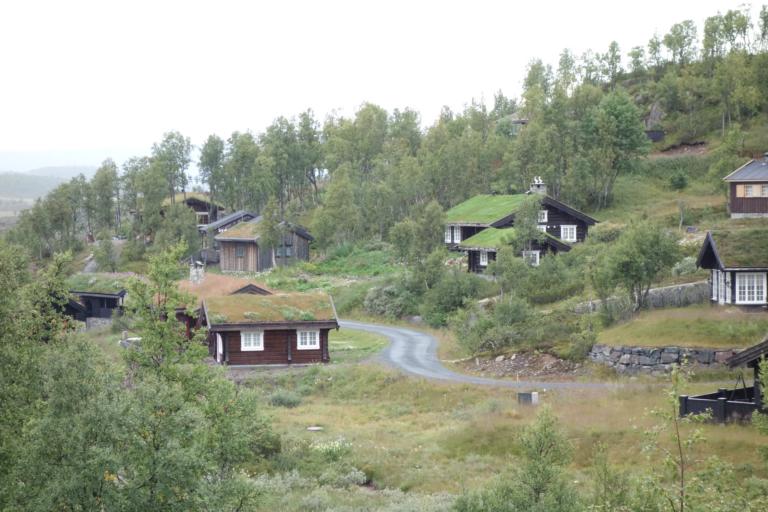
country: NO
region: Telemark
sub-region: Vinje
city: Amot
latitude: 59.7471
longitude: 8.1749
